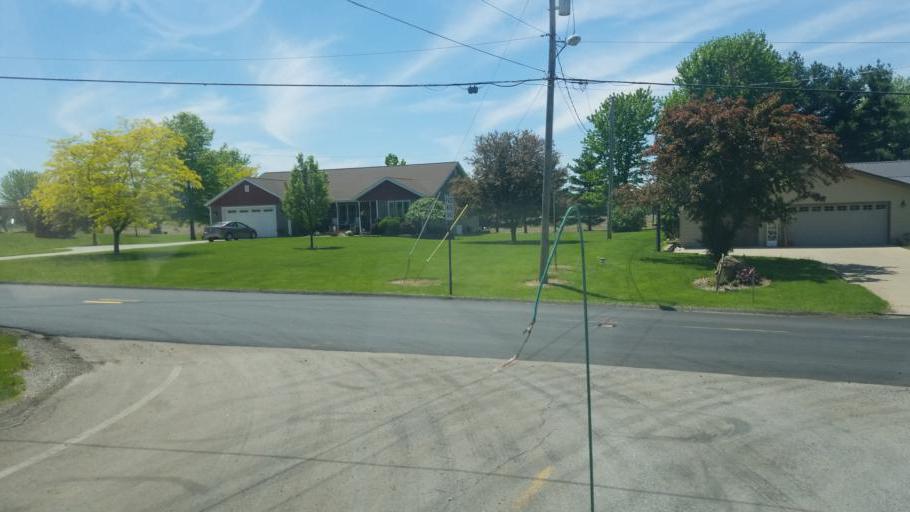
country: US
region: Ohio
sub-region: Huron County
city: Norwalk
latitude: 41.2074
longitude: -82.5902
